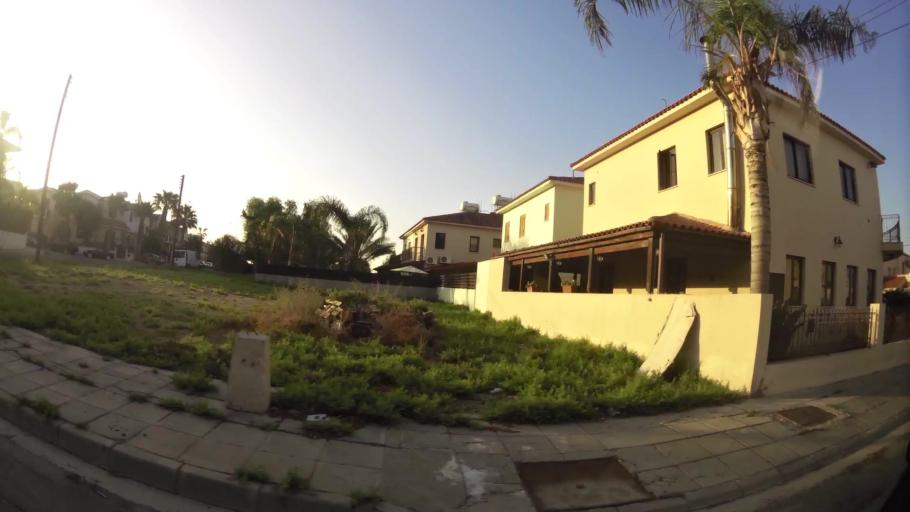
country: CY
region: Larnaka
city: Aradippou
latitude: 34.9242
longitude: 33.5957
